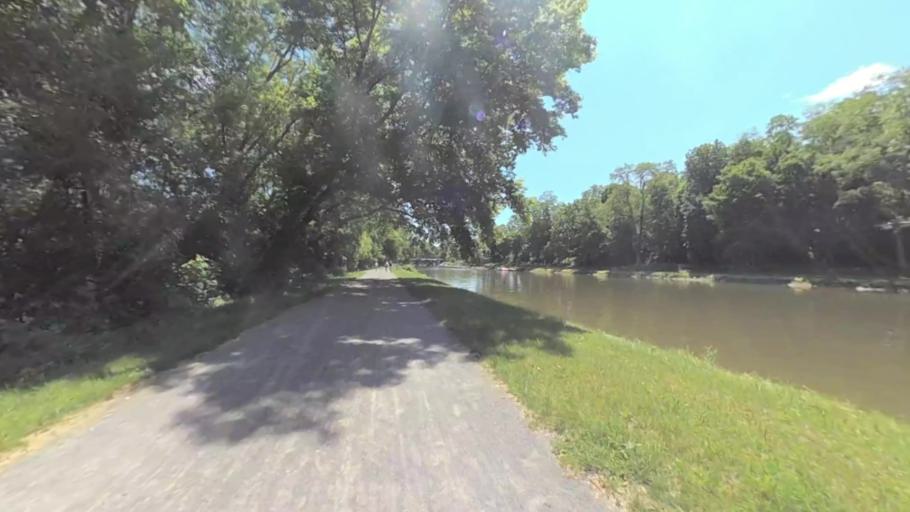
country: US
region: New York
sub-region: Monroe County
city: Pittsford
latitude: 43.0630
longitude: -77.4805
